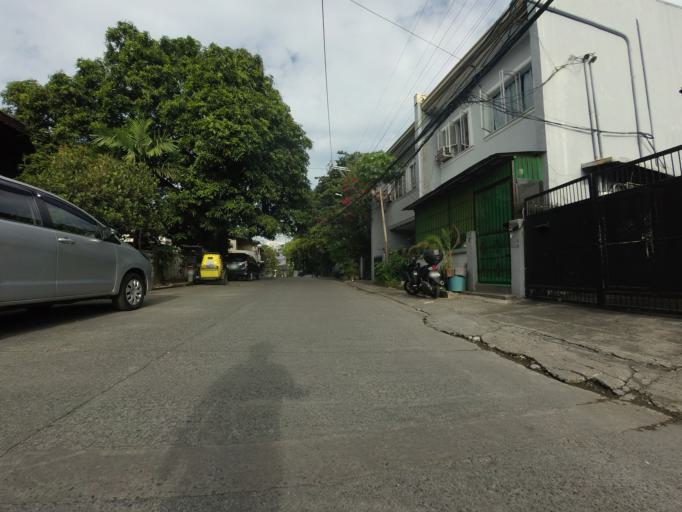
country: PH
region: Metro Manila
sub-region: Pasig
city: Pasig City
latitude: 14.5700
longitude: 121.0603
